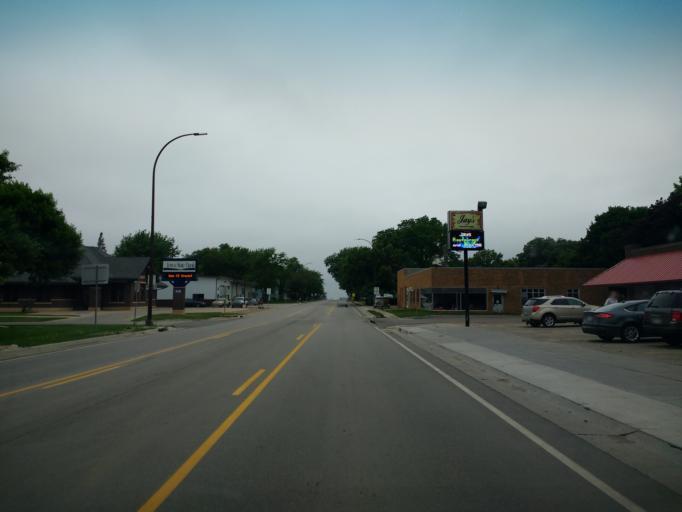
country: US
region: Iowa
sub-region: O'Brien County
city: Sanborn
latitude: 43.1861
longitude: -95.6568
